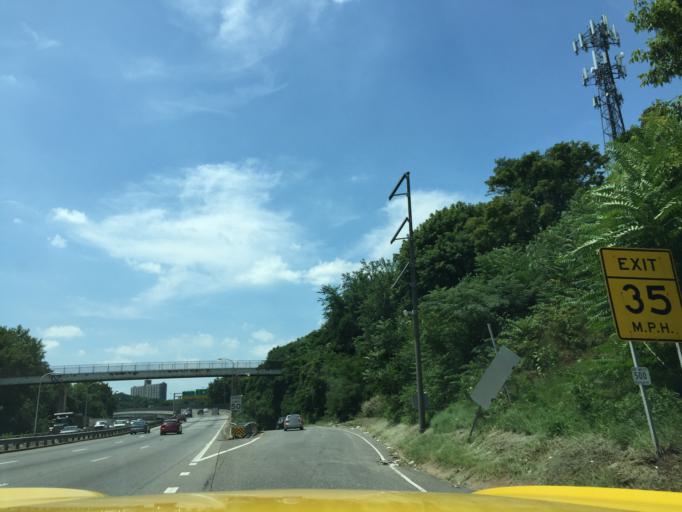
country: US
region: Pennsylvania
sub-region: Montgomery County
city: Bala-Cynwyd
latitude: 40.0098
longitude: -75.1872
